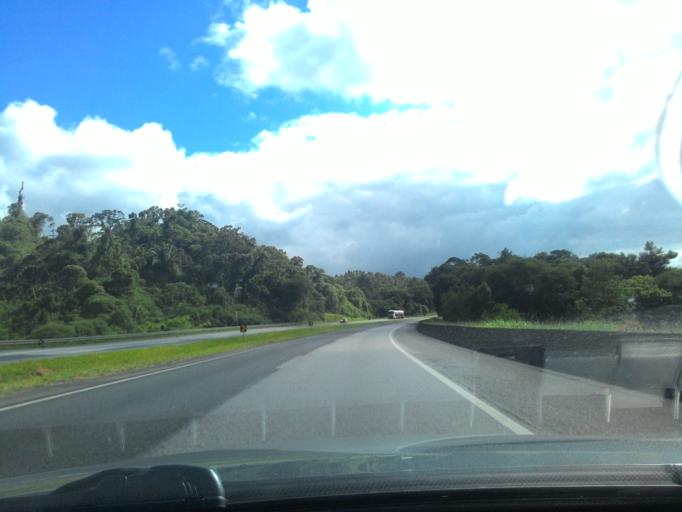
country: BR
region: Sao Paulo
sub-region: Cajati
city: Cajati
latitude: -24.9499
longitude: -48.3152
